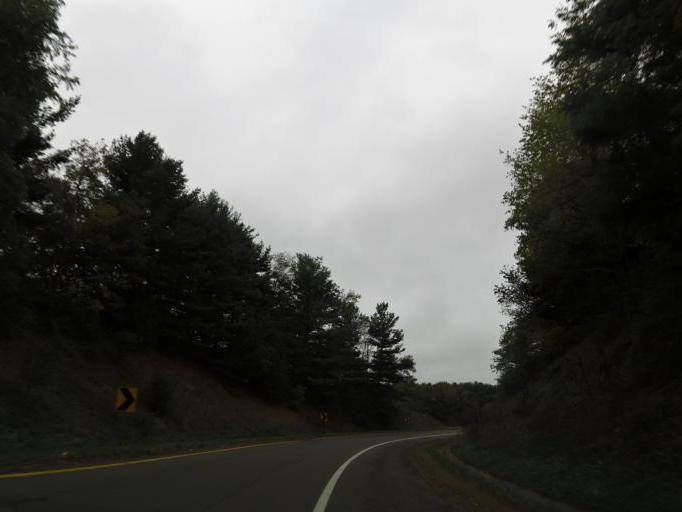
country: US
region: Virginia
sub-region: Wythe County
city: Wytheville
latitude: 36.9629
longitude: -81.0664
